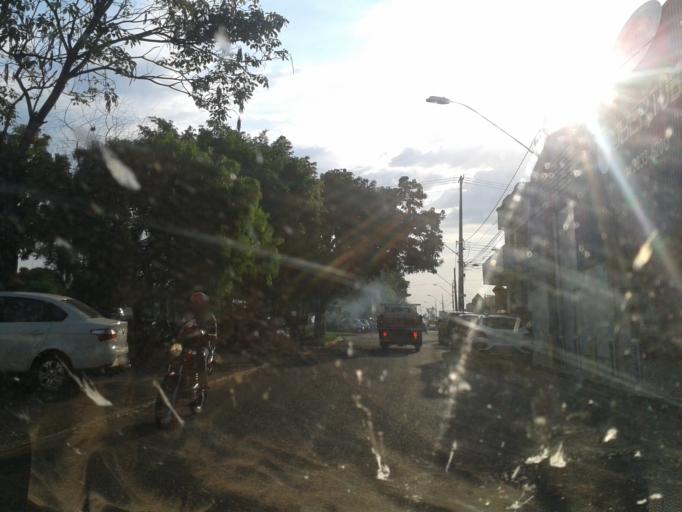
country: BR
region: Minas Gerais
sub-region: Uberlandia
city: Uberlandia
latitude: -18.9394
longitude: -48.3100
